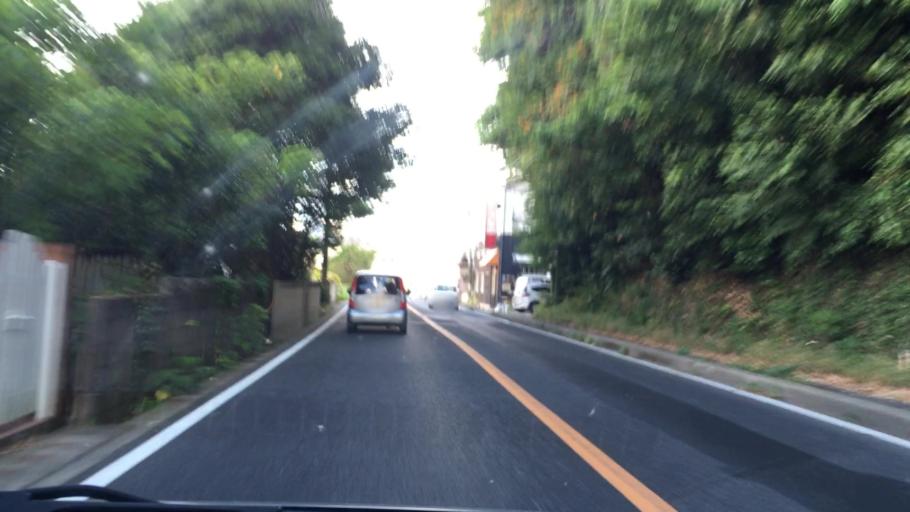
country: JP
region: Nagasaki
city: Sasebo
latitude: 33.1344
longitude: 129.7952
